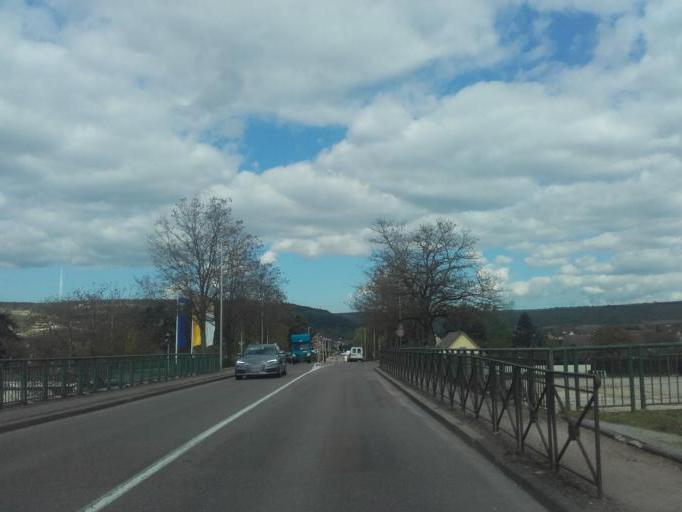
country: FR
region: Bourgogne
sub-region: Departement de la Cote-d'Or
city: Nuits-Saint-Georges
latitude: 47.1346
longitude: 4.9592
